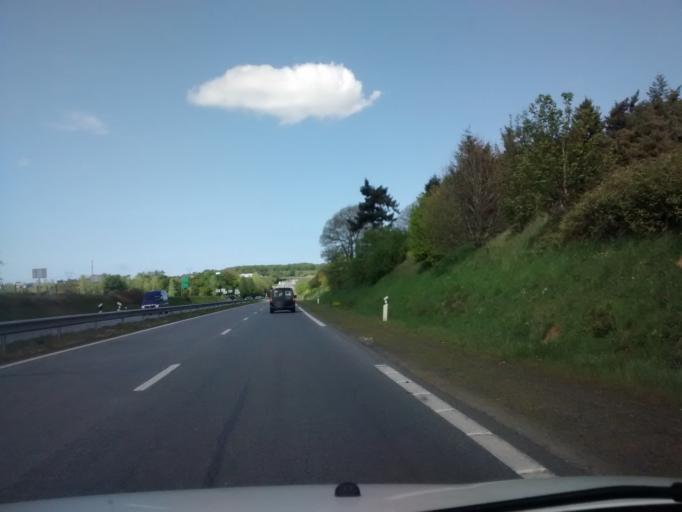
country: FR
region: Brittany
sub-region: Departement des Cotes-d'Armor
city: Saint-Samson-sur-Rance
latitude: 48.5113
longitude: -2.0392
